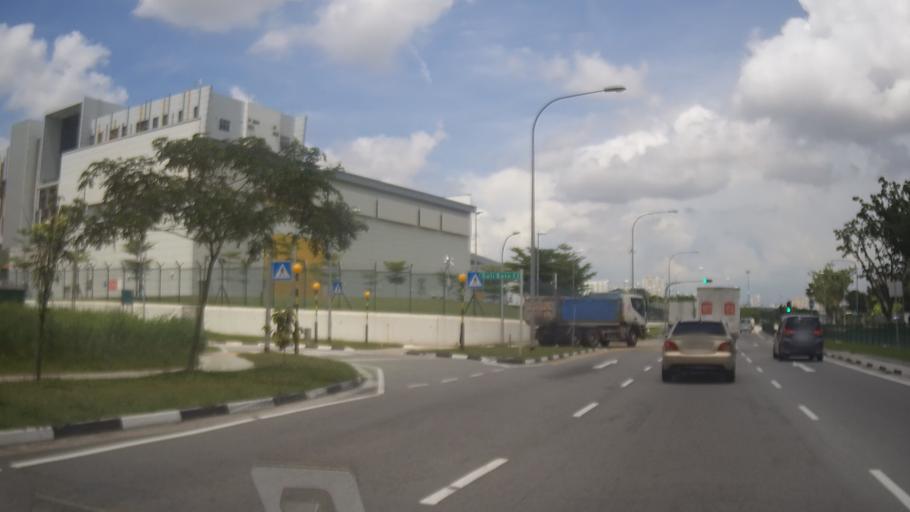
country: MY
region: Johor
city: Johor Bahru
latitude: 1.4046
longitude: 103.7563
